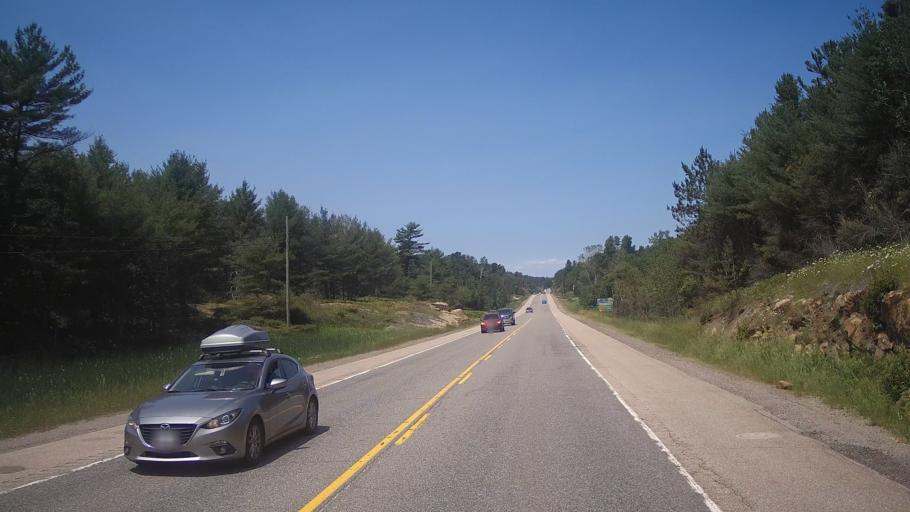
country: CA
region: Ontario
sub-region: Parry Sound District
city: Parry Sound
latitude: 45.5850
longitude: -80.3630
